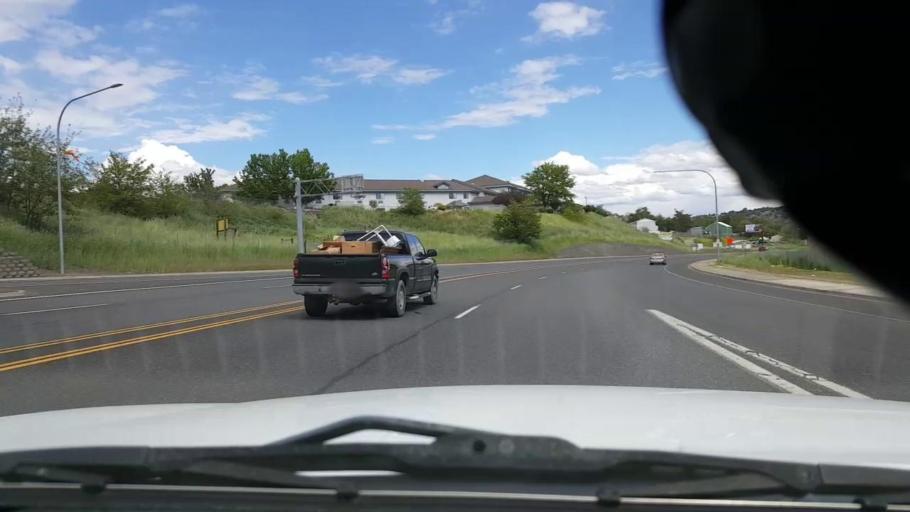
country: US
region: Washington
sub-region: Asotin County
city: West Clarkston-Highland
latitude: 46.4016
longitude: -117.0570
